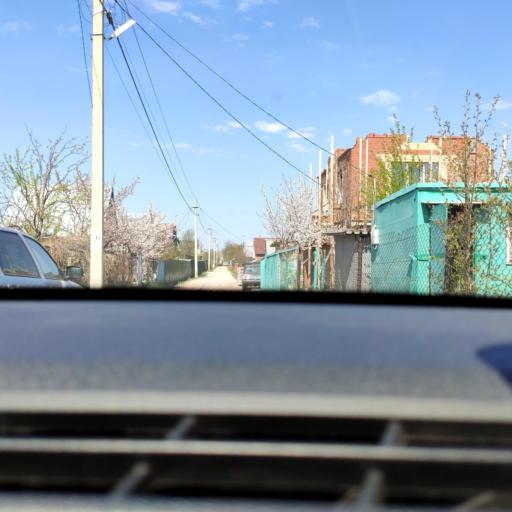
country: RU
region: Samara
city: Tol'yatti
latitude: 53.5934
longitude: 49.3008
